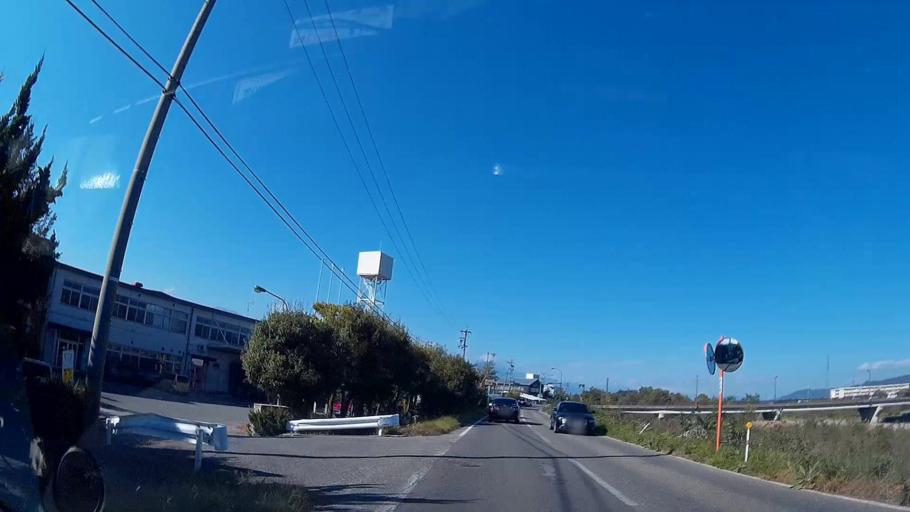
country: JP
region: Nagano
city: Matsumoto
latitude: 36.2037
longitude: 137.9434
